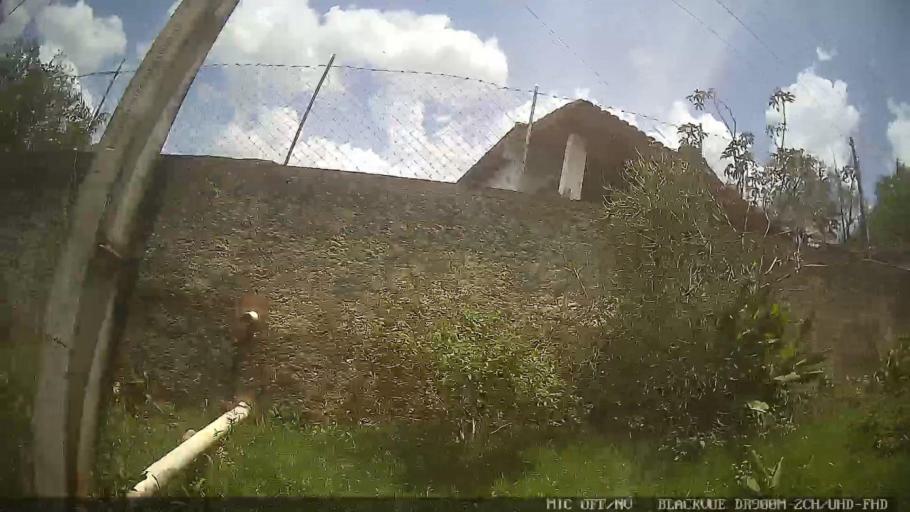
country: BR
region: Sao Paulo
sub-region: Braganca Paulista
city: Braganca Paulista
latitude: -23.0347
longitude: -46.5322
